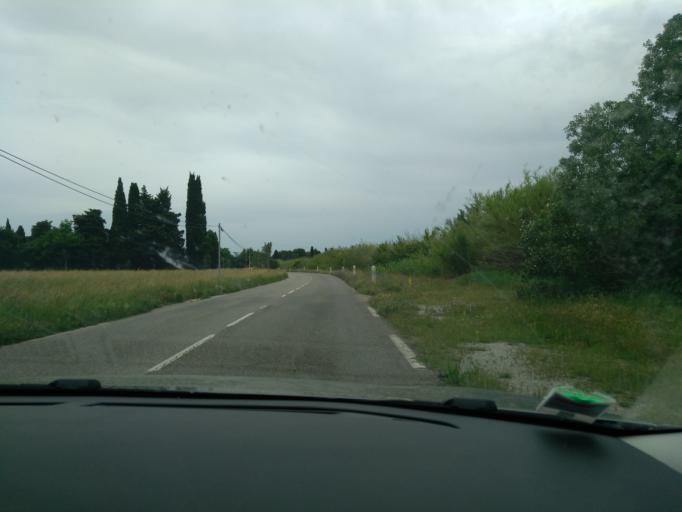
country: FR
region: Provence-Alpes-Cote d'Azur
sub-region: Departement des Bouches-du-Rhone
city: Eyguieres
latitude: 43.6489
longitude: 5.0192
